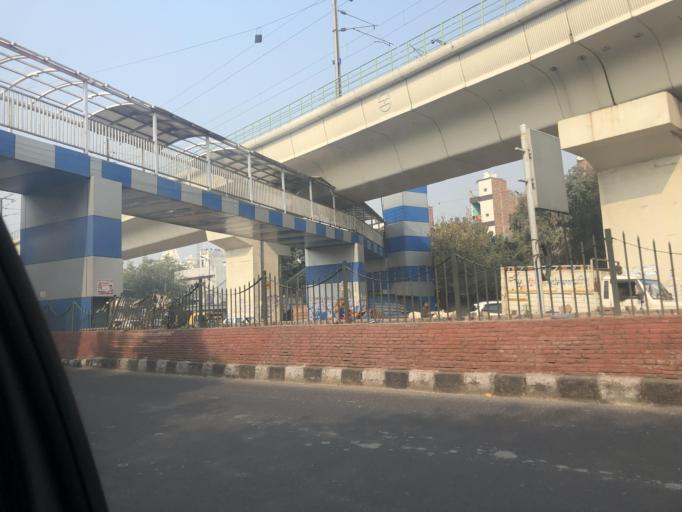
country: IN
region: NCT
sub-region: West Delhi
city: Nangloi Jat
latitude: 28.6821
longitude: 77.0716
